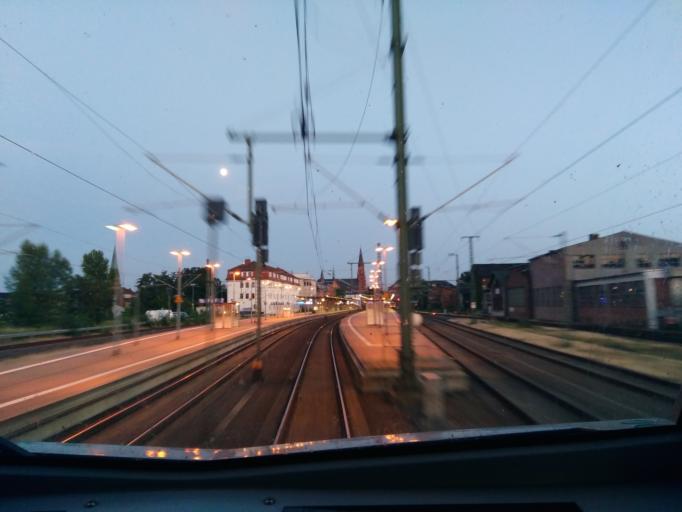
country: DE
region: Mecklenburg-Vorpommern
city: Paulsstadt
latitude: 53.6372
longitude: 11.4073
